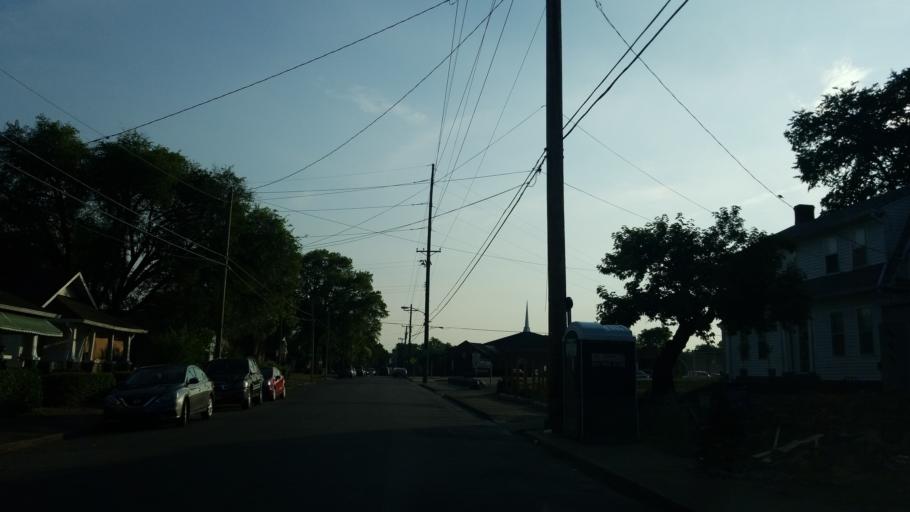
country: US
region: Tennessee
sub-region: Davidson County
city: Nashville
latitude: 36.1685
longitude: -86.7988
